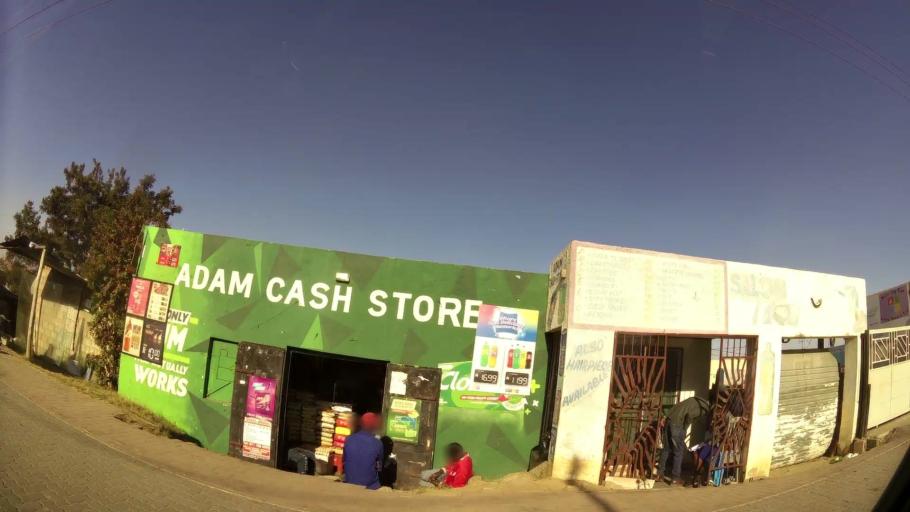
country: ZA
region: Gauteng
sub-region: City of Johannesburg Metropolitan Municipality
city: Diepsloot
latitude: -25.9280
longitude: 28.0064
